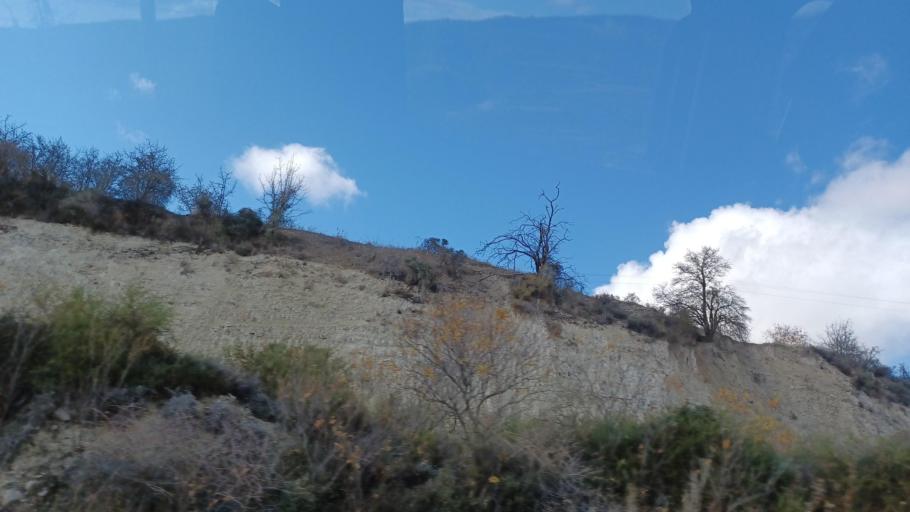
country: CY
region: Limassol
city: Pachna
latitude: 34.8417
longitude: 32.8081
